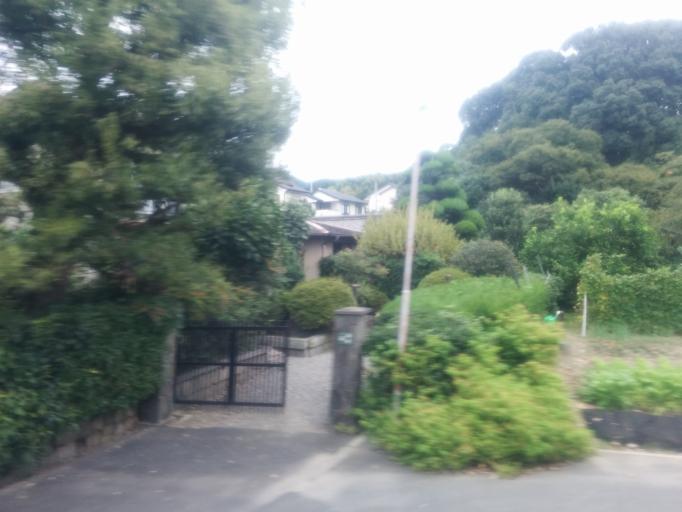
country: JP
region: Kyoto
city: Kyoto
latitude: 34.9598
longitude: 135.7757
